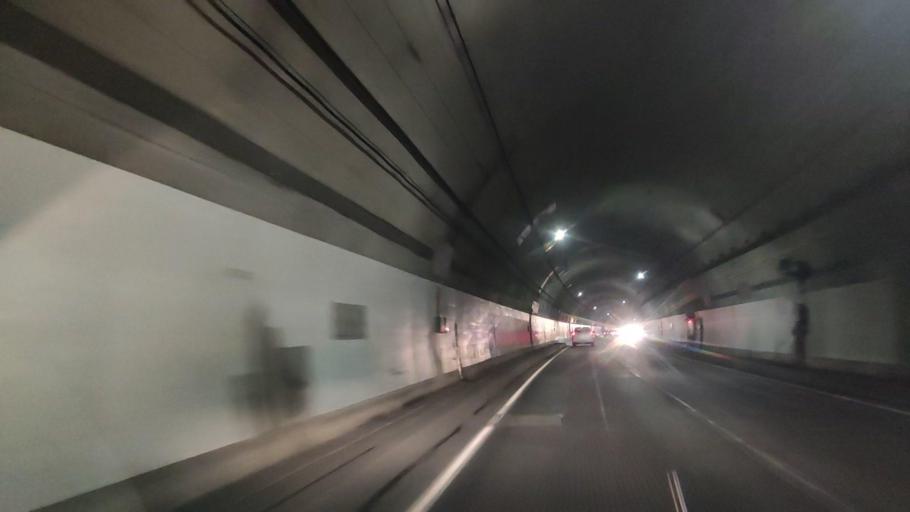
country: JP
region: Hokkaido
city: Rumoi
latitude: 43.7032
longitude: 141.3363
